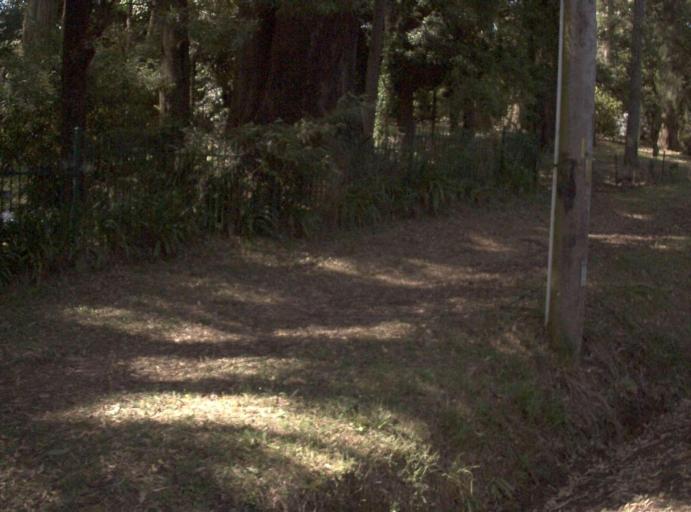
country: AU
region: Victoria
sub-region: Yarra Ranges
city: Mount Dandenong
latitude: -37.8330
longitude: 145.3513
